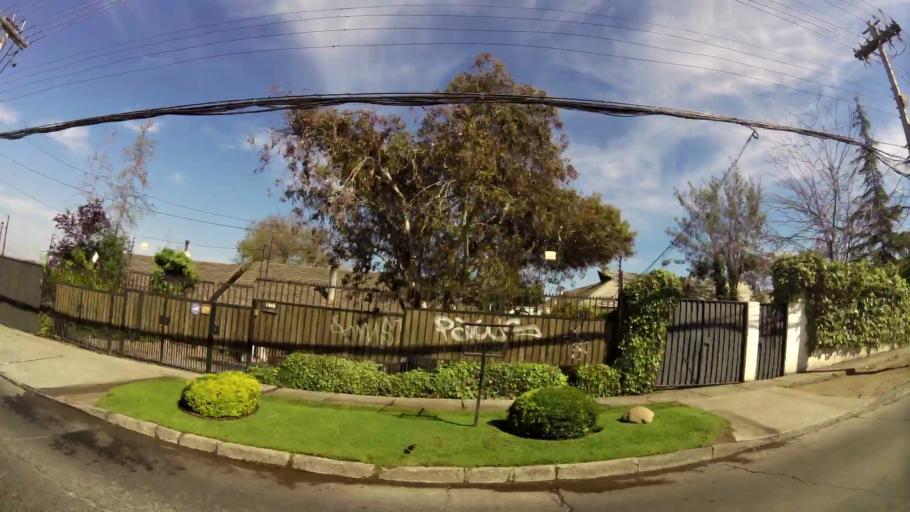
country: CL
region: Santiago Metropolitan
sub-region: Provincia de Santiago
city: Villa Presidente Frei, Nunoa, Santiago, Chile
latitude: -33.4396
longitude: -70.5332
